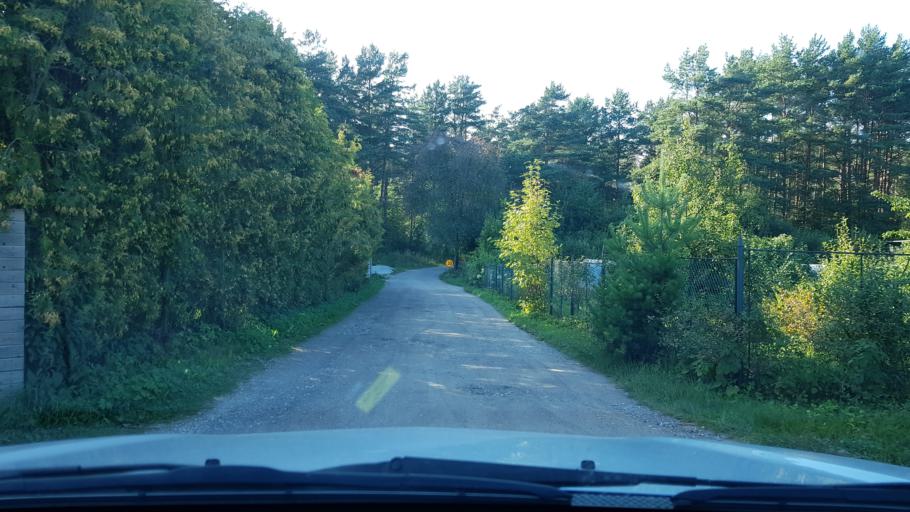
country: EE
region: Ida-Virumaa
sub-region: Narva-Joesuu linn
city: Narva-Joesuu
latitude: 59.4457
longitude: 28.0734
